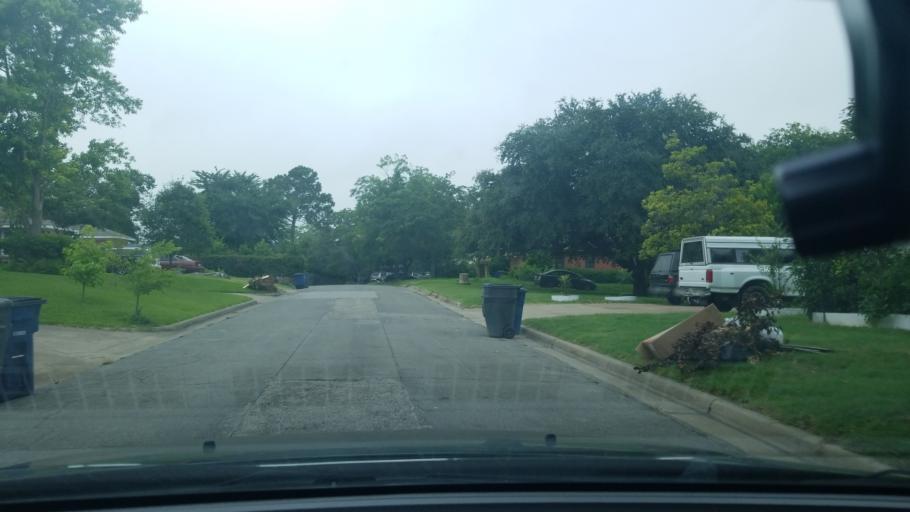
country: US
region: Texas
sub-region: Dallas County
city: Balch Springs
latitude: 32.7592
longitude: -96.6935
